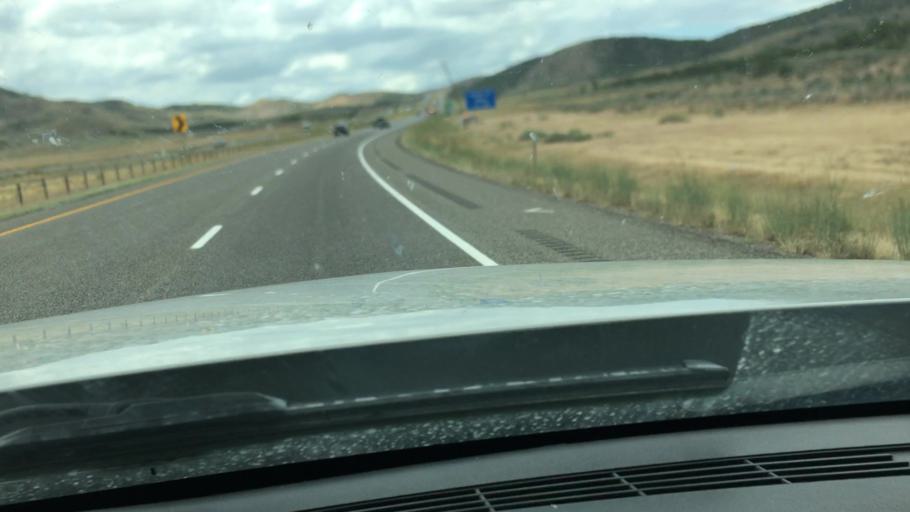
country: US
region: Utah
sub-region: Beaver County
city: Beaver
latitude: 38.6664
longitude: -112.5910
